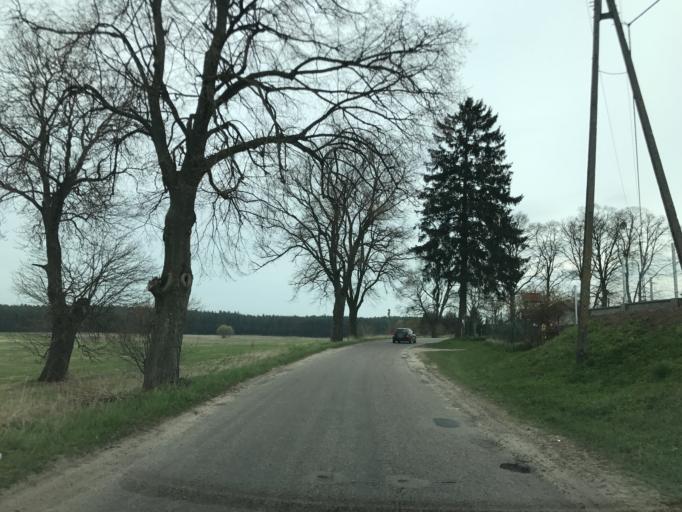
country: PL
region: Warmian-Masurian Voivodeship
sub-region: Powiat olsztynski
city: Olsztynek
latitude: 53.6010
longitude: 20.2703
